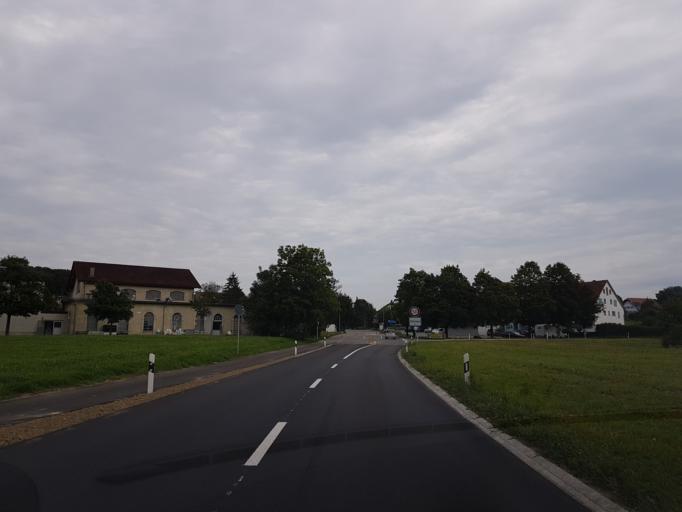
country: CH
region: Zurich
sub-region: Bezirk Affoltern
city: Obfelden / Oberlunnern
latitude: 47.2645
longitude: 8.4056
